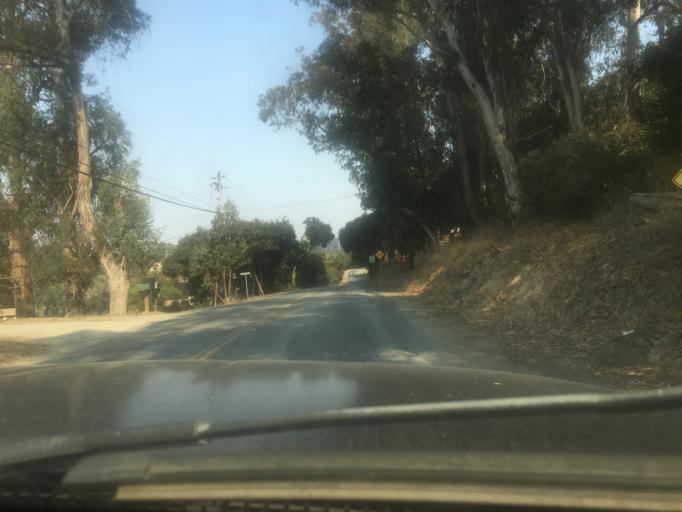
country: US
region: California
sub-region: Monterey County
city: Prunedale
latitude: 36.7774
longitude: -121.6573
